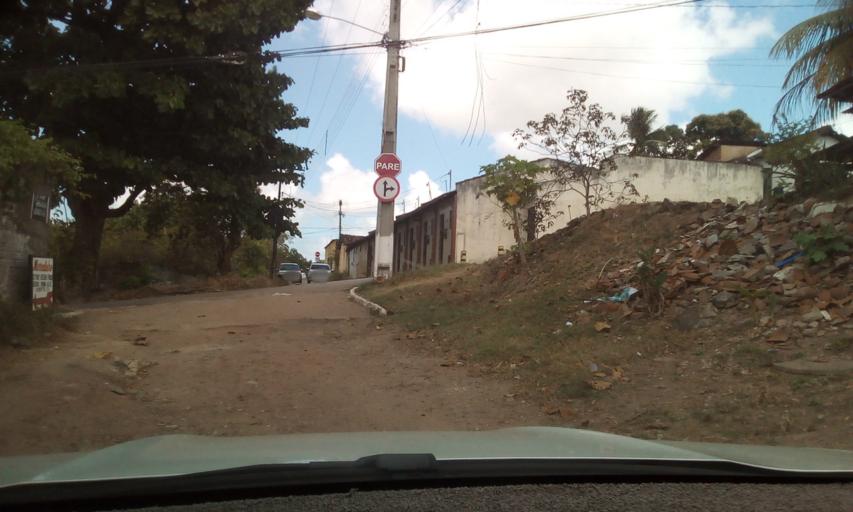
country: BR
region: Paraiba
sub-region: Joao Pessoa
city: Joao Pessoa
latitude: -7.1422
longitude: -34.8766
